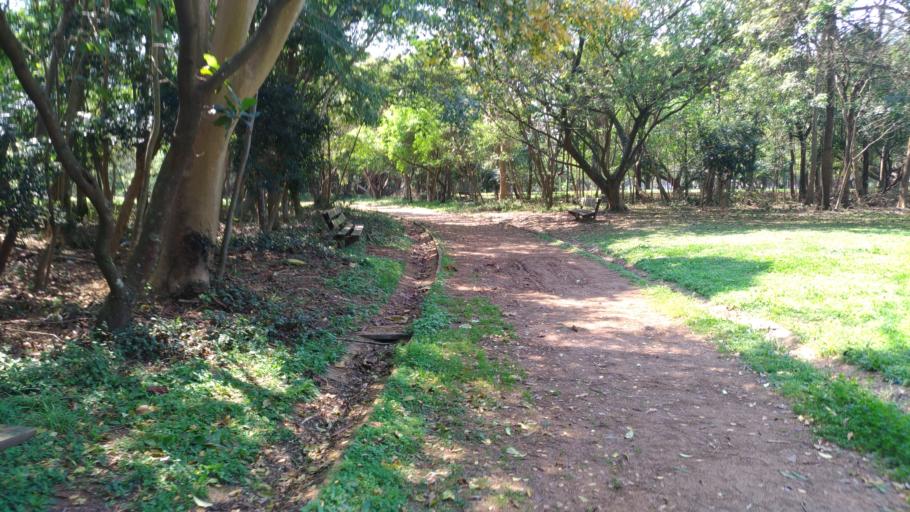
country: BR
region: Sao Paulo
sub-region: Osasco
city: Osasco
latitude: -23.5462
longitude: -46.7214
